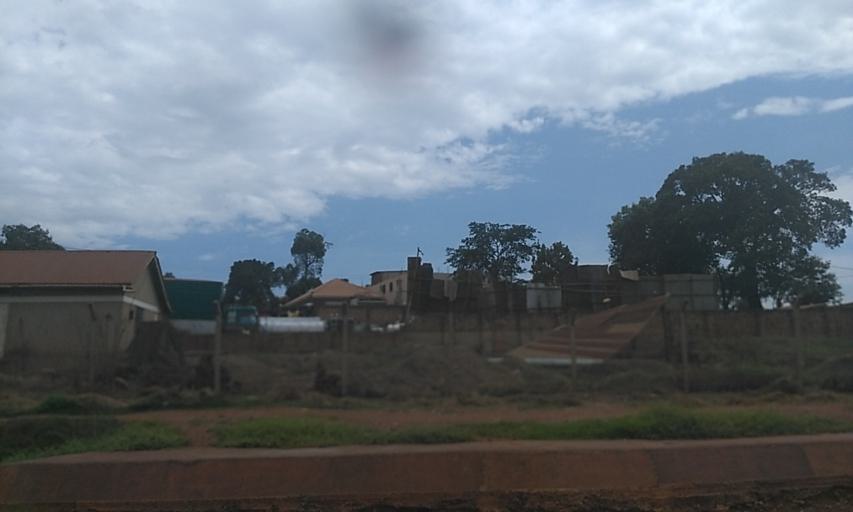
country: UG
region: Central Region
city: Kampala Central Division
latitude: 0.3325
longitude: 32.5279
